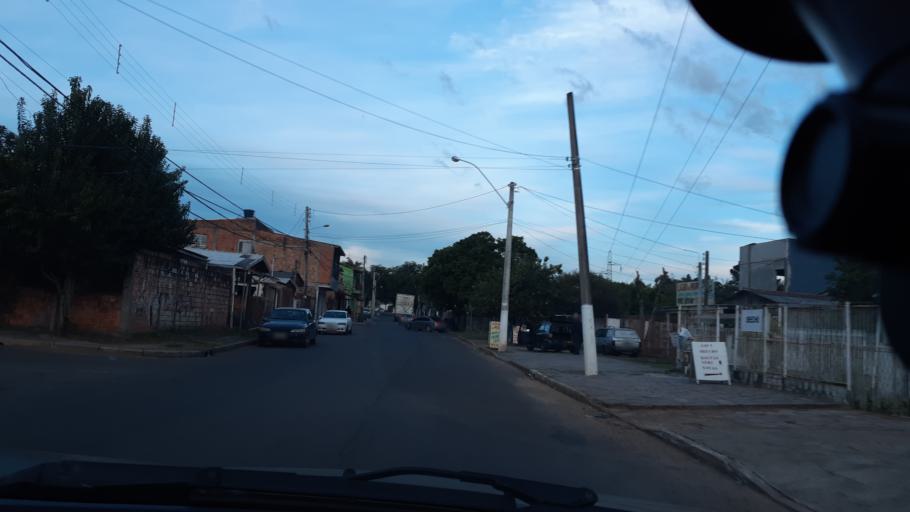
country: BR
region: Rio Grande do Sul
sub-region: Sapucaia Do Sul
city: Sapucaia
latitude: -29.8423
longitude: -51.1532
